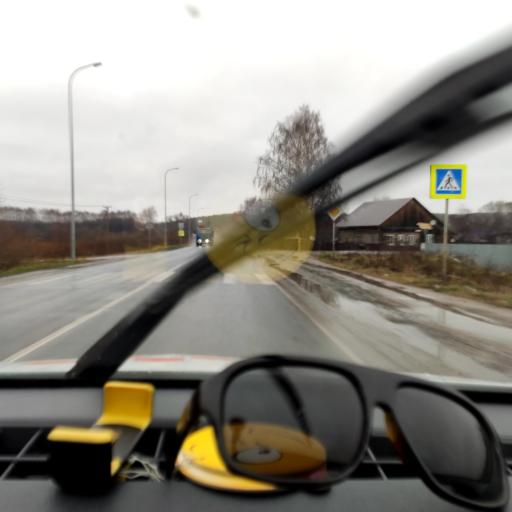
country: RU
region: Bashkortostan
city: Iglino
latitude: 54.8306
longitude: 56.3911
